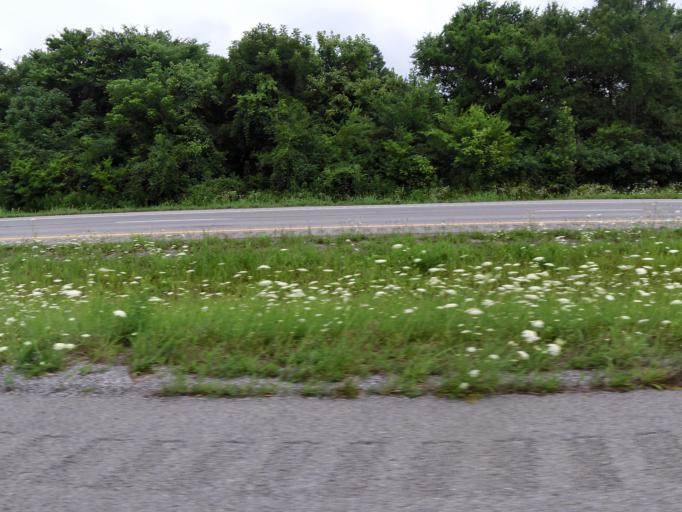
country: US
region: Kentucky
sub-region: Muhlenberg County
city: Central City
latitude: 37.3202
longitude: -87.0372
